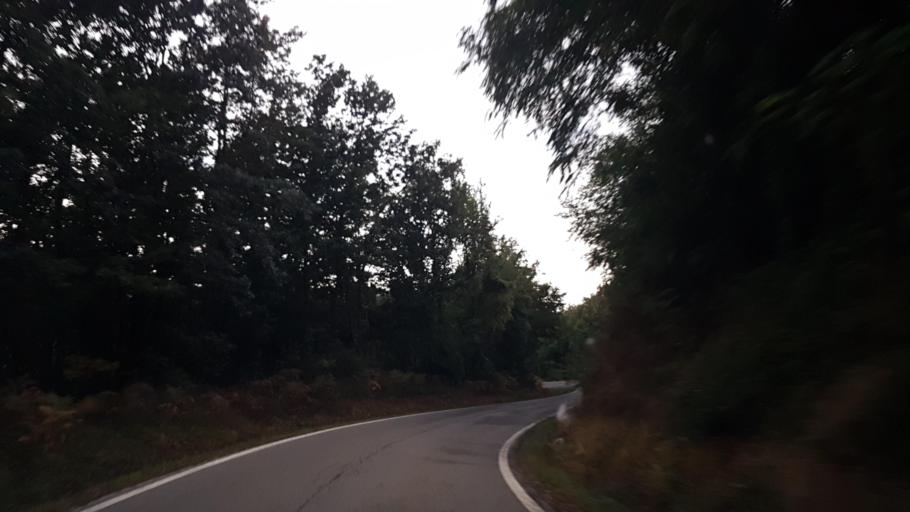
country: IT
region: Emilia-Romagna
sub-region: Provincia di Parma
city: Tornolo
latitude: 44.4365
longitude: 9.6341
